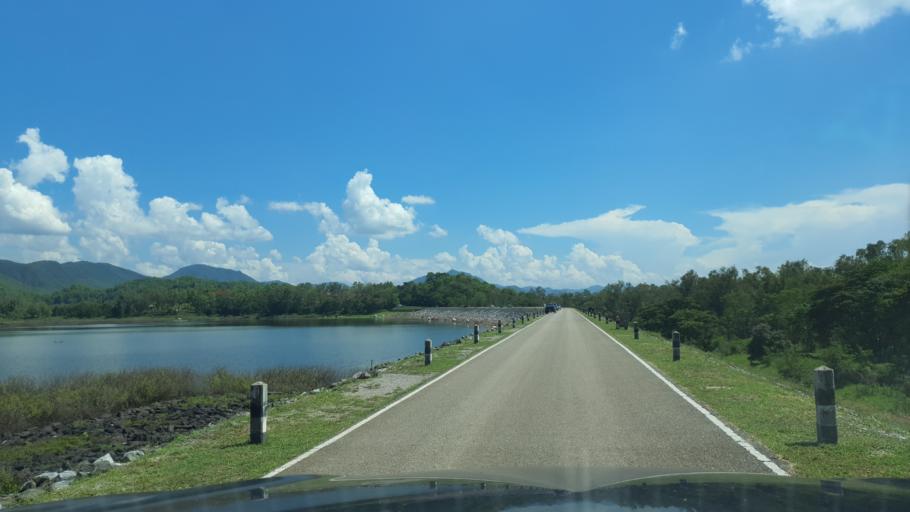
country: TH
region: Chiang Mai
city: Mae On
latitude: 18.8117
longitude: 99.2655
